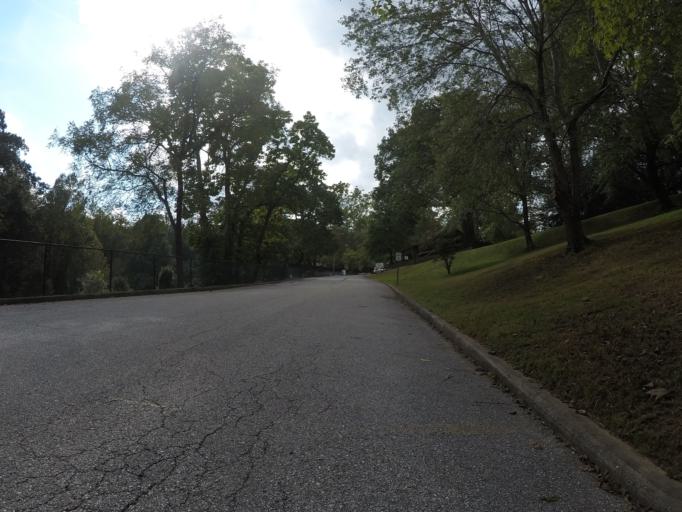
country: US
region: West Virginia
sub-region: Cabell County
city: Huntington
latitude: 38.4049
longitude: -82.4352
